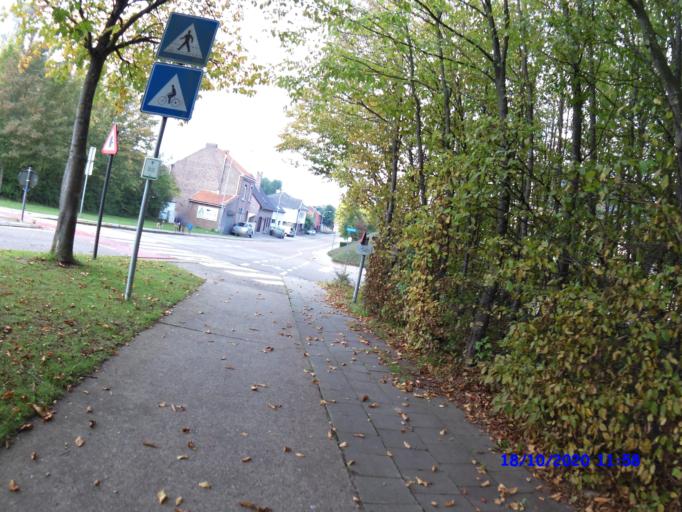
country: BE
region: Flanders
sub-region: Provincie Vlaams-Brabant
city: Landen
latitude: 50.7516
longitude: 5.0909
